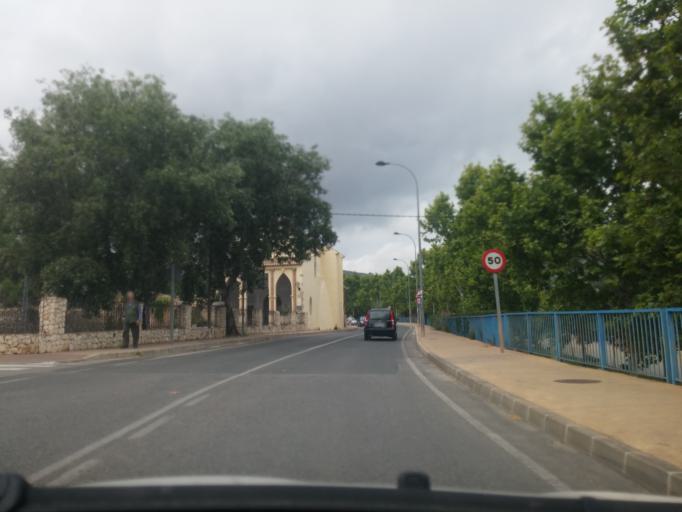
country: ES
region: Valencia
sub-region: Provincia de Alicante
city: Jalon
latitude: 38.7428
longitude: -0.0145
